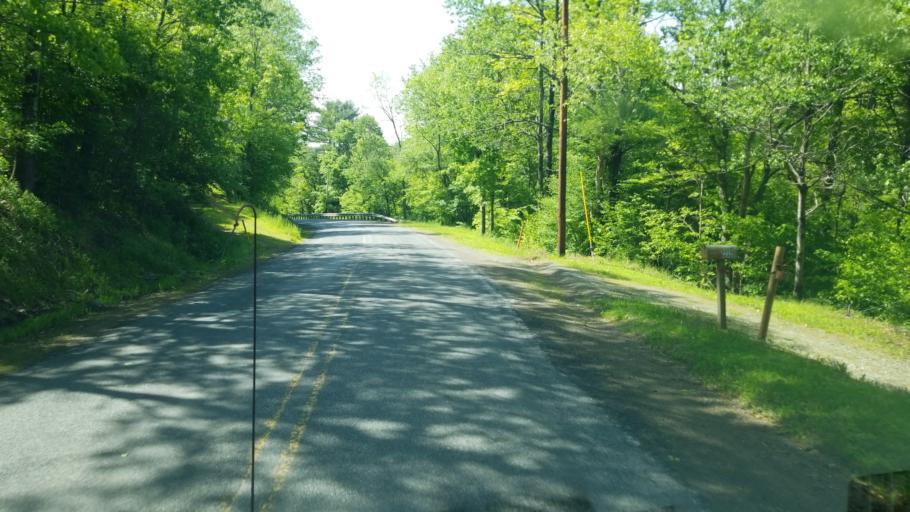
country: US
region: Pennsylvania
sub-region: Potter County
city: Galeton
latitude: 41.8534
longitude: -77.7085
